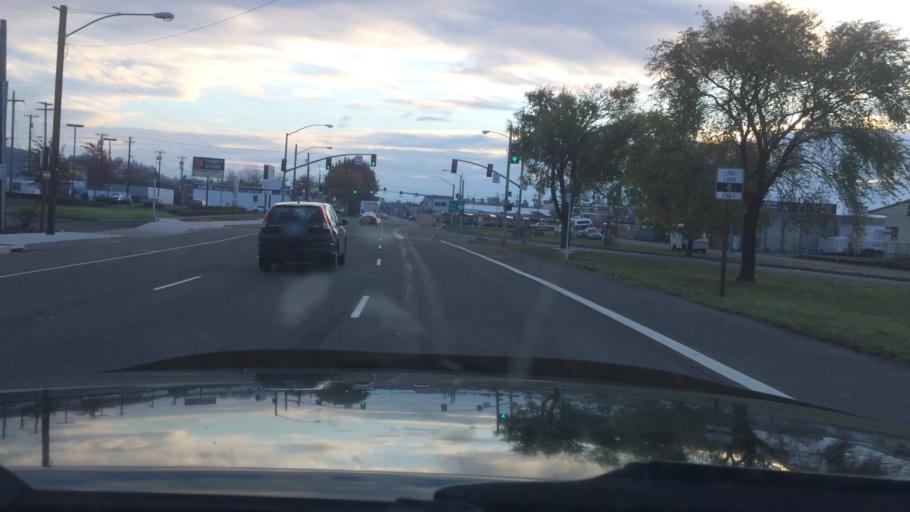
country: US
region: Oregon
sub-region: Lane County
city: Eugene
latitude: 44.0522
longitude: -123.1253
